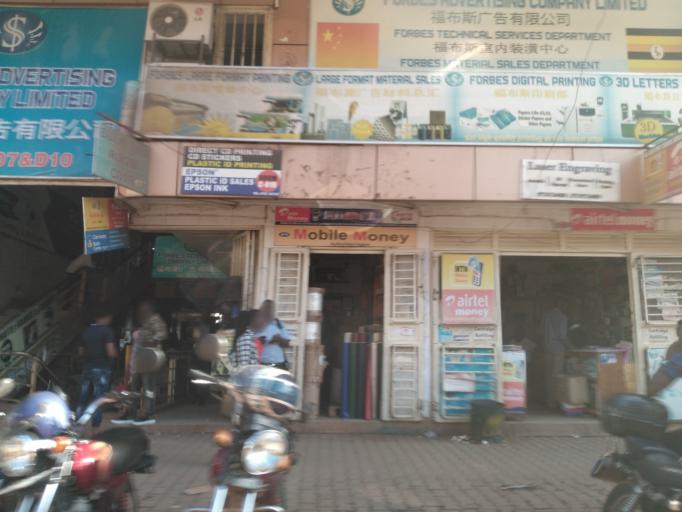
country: UG
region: Central Region
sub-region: Kampala District
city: Kampala
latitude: 0.3109
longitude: 32.5825
